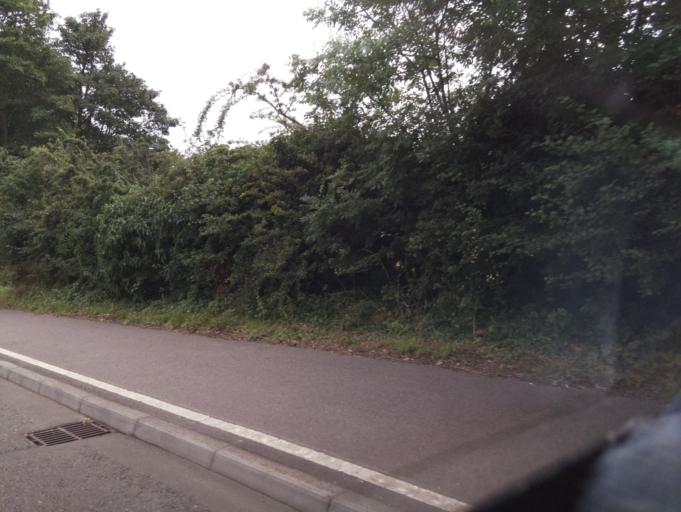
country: GB
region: England
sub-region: District of Rutland
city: Ryhall
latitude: 52.6673
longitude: -0.4682
